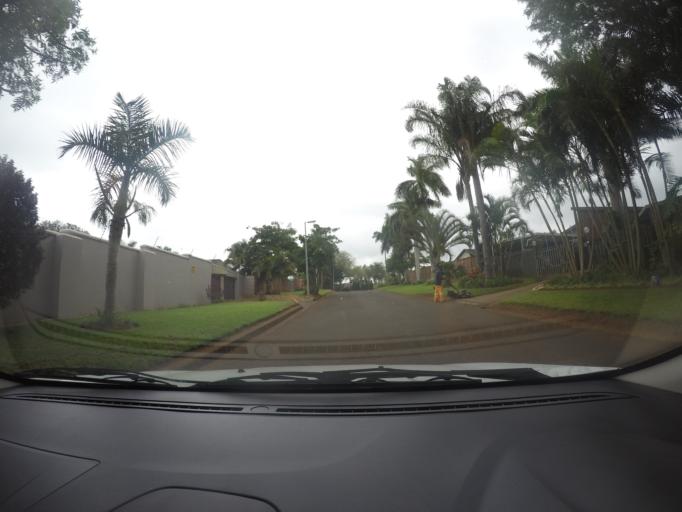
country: ZA
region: KwaZulu-Natal
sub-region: uThungulu District Municipality
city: Empangeni
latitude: -28.7649
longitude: 31.8967
